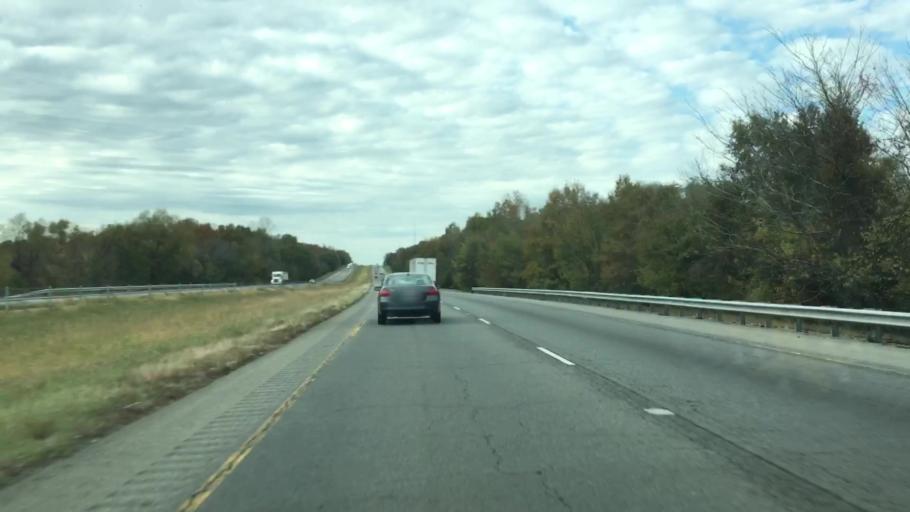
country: US
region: Arkansas
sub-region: Faulkner County
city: Conway
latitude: 35.1392
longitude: -92.5241
